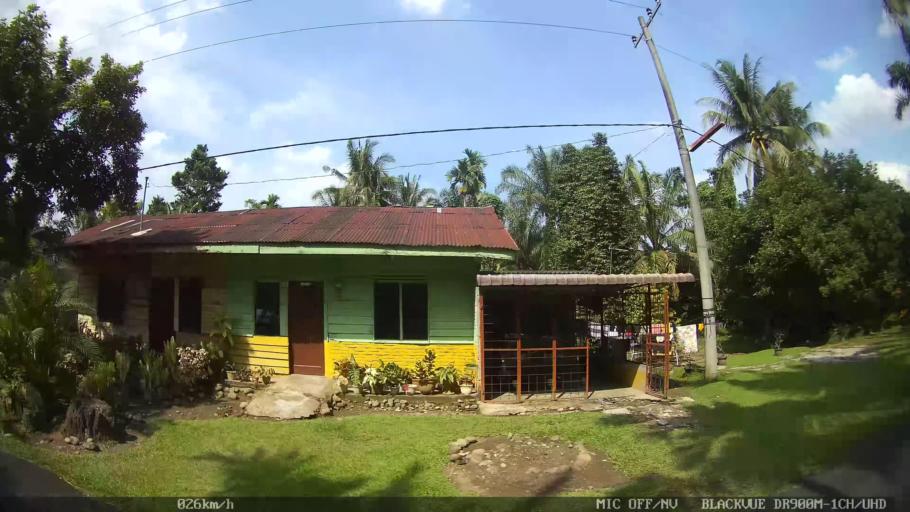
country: ID
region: North Sumatra
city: Binjai
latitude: 3.6345
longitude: 98.5214
